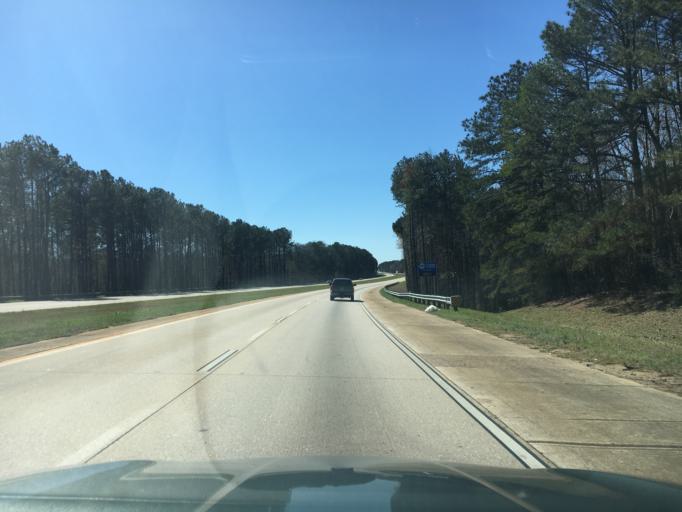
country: US
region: Georgia
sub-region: Troup County
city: La Grange
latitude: 33.0161
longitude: -84.9898
